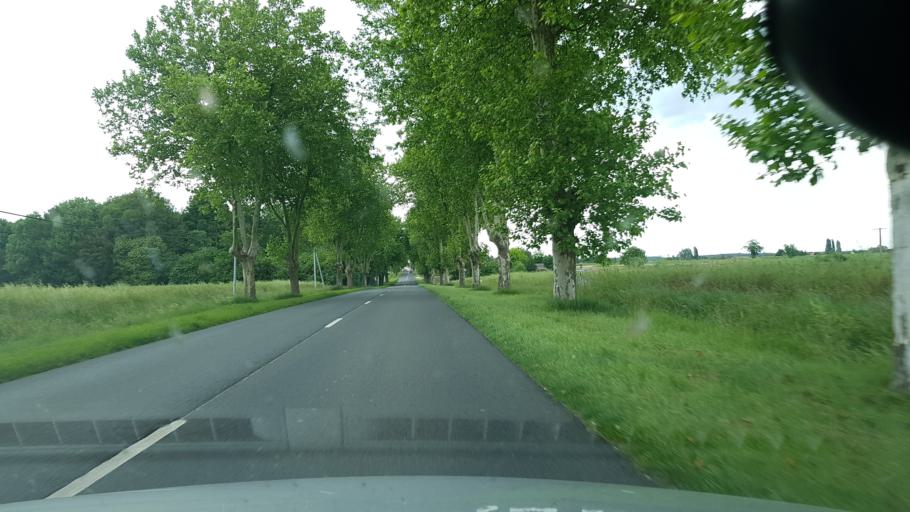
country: FR
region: Centre
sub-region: Departement du Loir-et-Cher
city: Chatillon-sur-Cher
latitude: 47.3359
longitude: 1.4850
